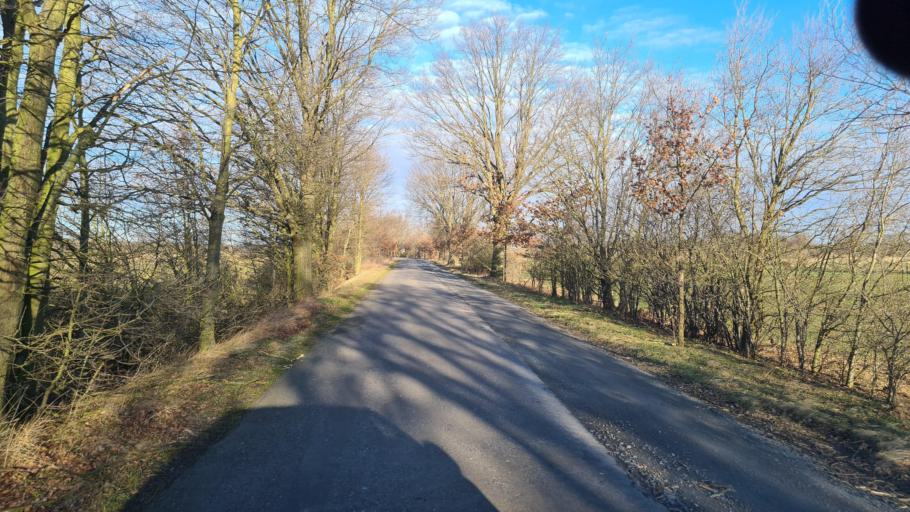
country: DE
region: Brandenburg
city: Herzberg
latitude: 51.7069
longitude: 13.2132
